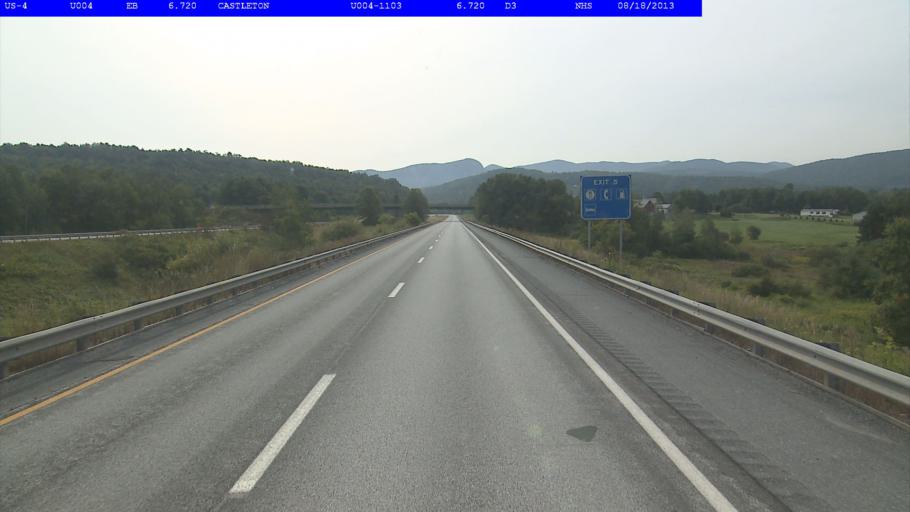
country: US
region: Vermont
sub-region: Rutland County
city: Castleton
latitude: 43.6206
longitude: -73.1848
